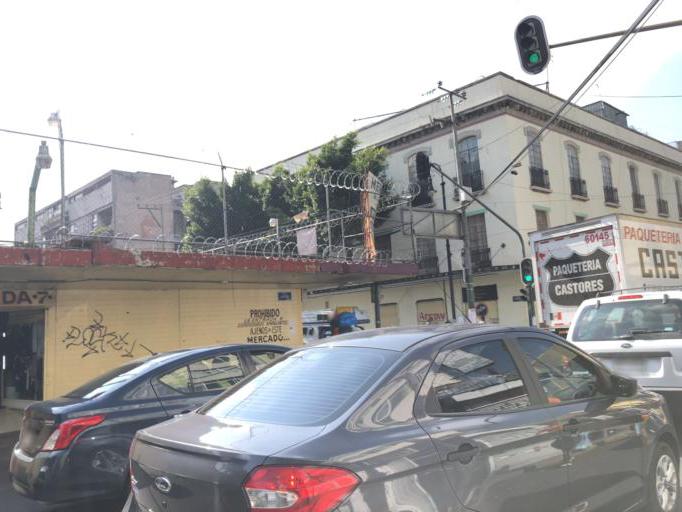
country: MX
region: Mexico City
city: Cuauhtemoc
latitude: 19.4428
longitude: -99.1371
